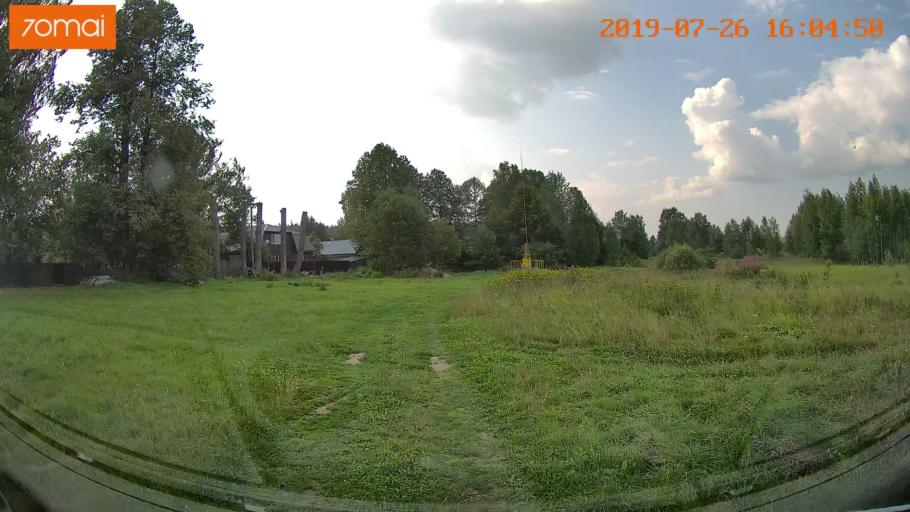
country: RU
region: Ivanovo
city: Bogorodskoye
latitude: 57.0573
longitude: 41.0582
